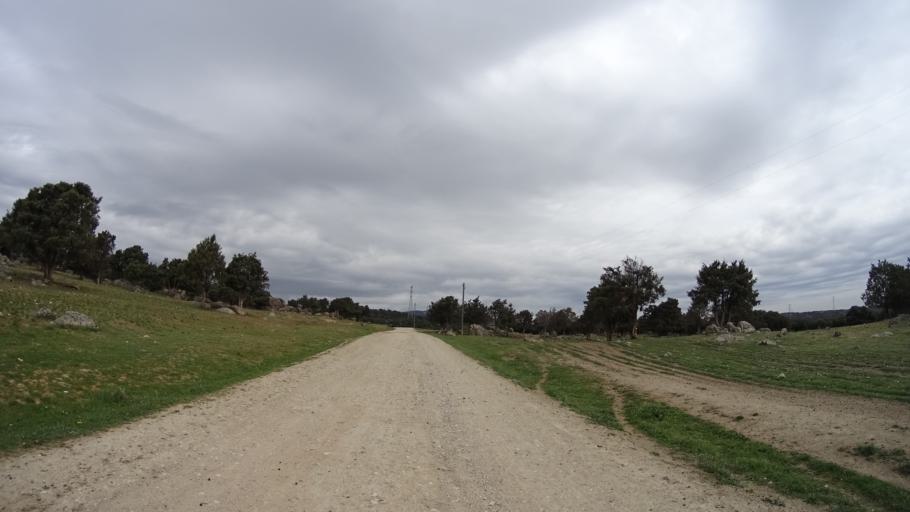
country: ES
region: Madrid
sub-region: Provincia de Madrid
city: Hoyo de Manzanares
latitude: 40.6081
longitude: -3.8773
